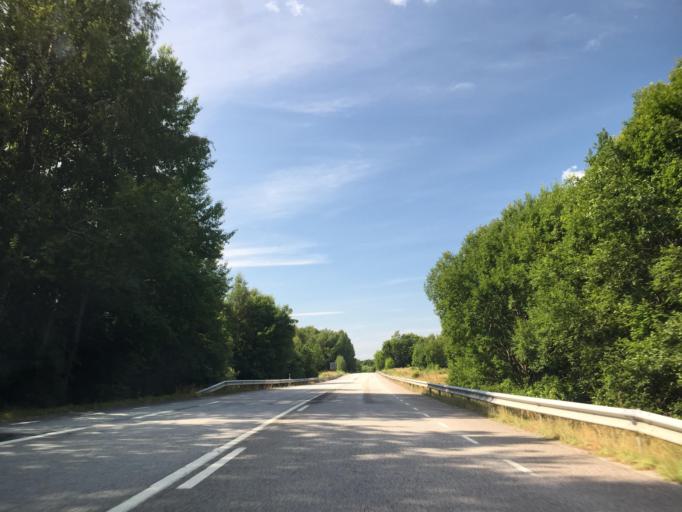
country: SE
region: Vaestra Goetaland
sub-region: Tanums Kommun
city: Grebbestad
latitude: 58.7603
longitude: 11.2608
